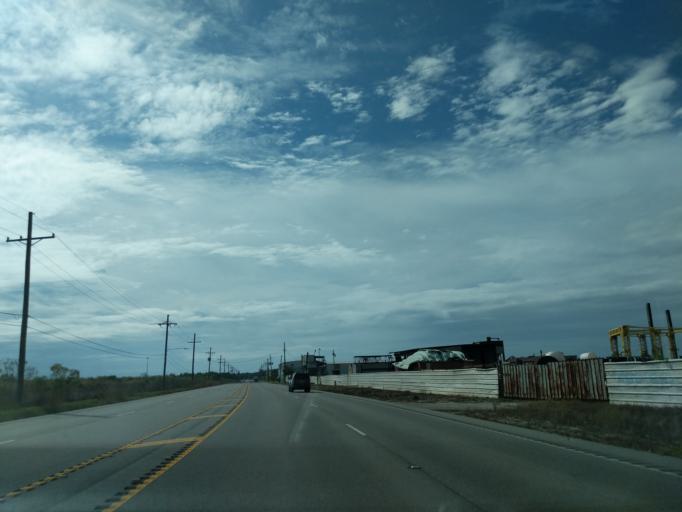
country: US
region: Louisiana
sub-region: Saint Tammany Parish
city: Eden Isle
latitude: 30.0770
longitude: -89.8464
